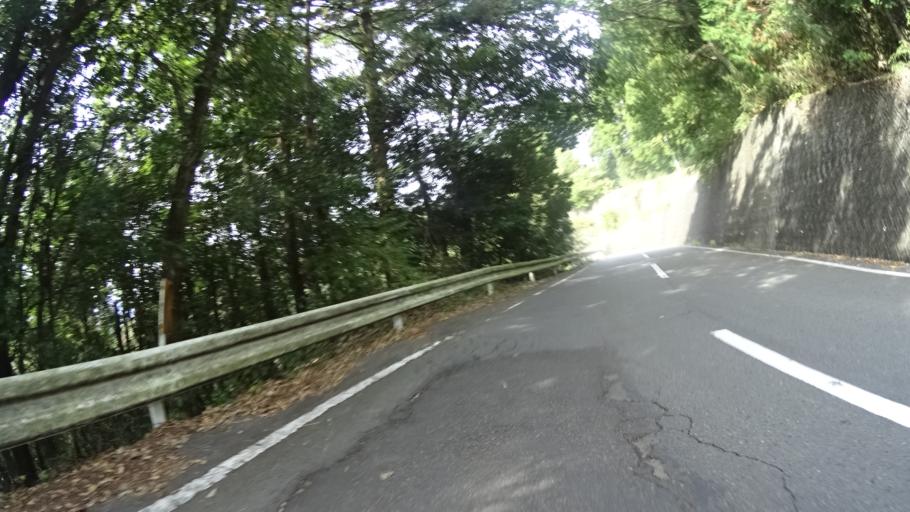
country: JP
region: Yamanashi
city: Uenohara
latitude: 35.6256
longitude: 139.0287
